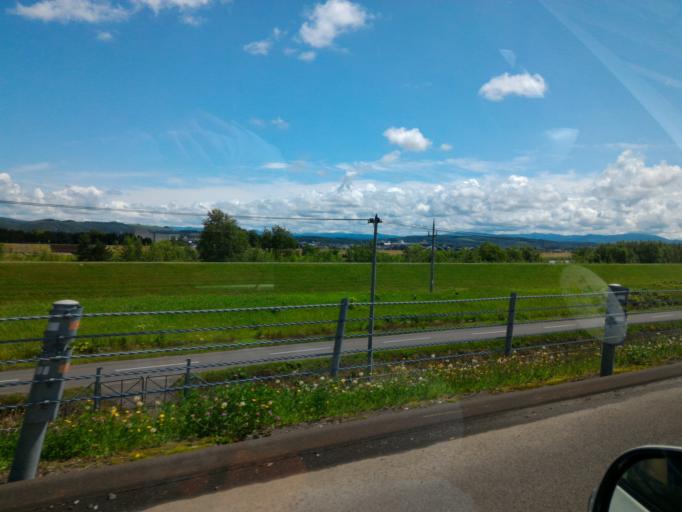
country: JP
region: Hokkaido
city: Nayoro
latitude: 44.3540
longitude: 142.4359
